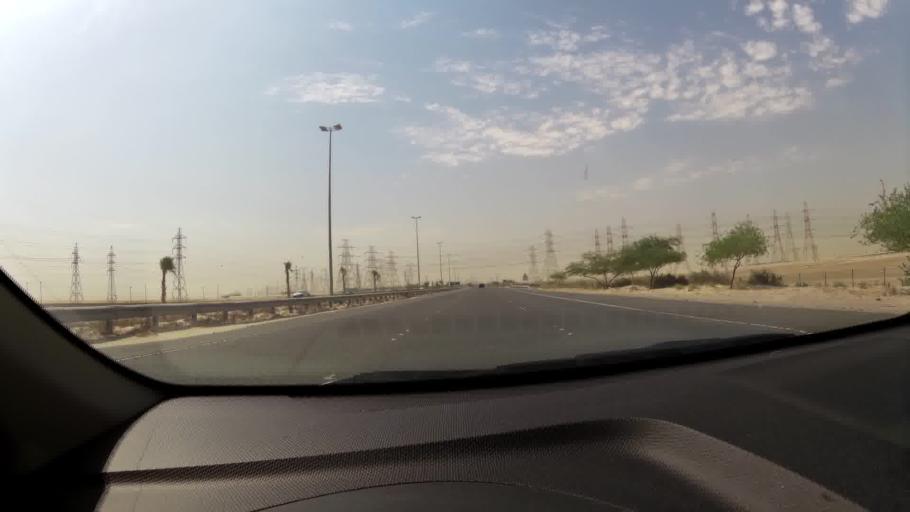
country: KW
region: Al Ahmadi
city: Al Fahahil
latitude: 28.7617
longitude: 48.2793
